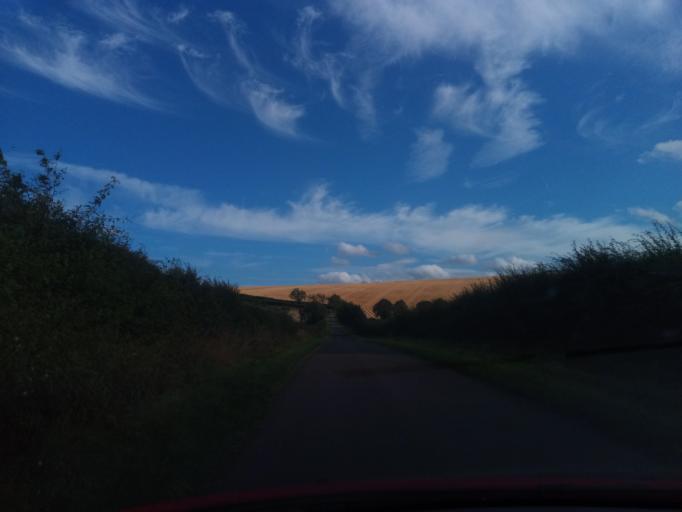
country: GB
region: Scotland
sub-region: The Scottish Borders
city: Coldstream
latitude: 55.6205
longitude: -2.1928
